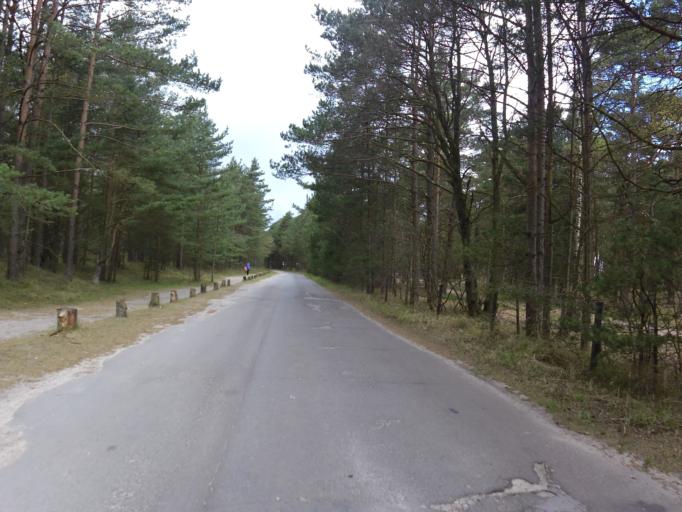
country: DE
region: Mecklenburg-Vorpommern
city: Ostseebad Prerow
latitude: 54.4550
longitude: 12.5448
